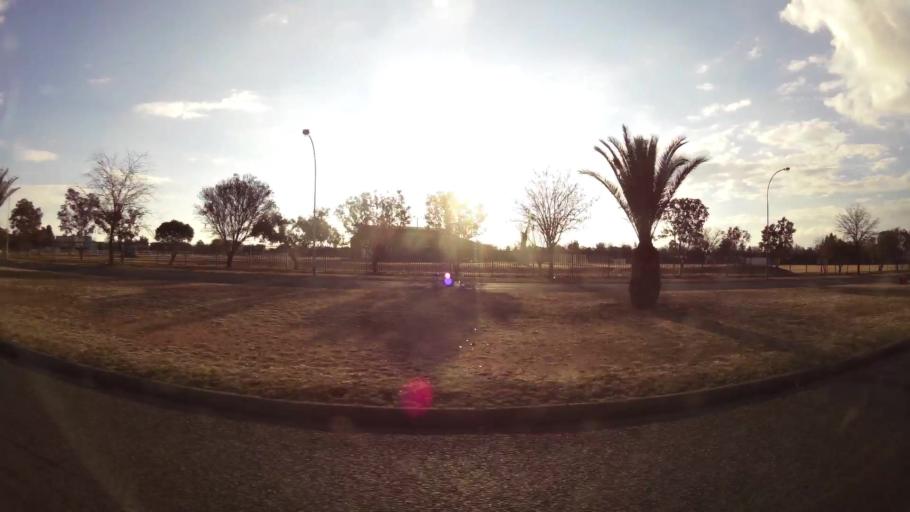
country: ZA
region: Orange Free State
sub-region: Mangaung Metropolitan Municipality
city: Bloemfontein
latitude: -29.1484
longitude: 26.1873
